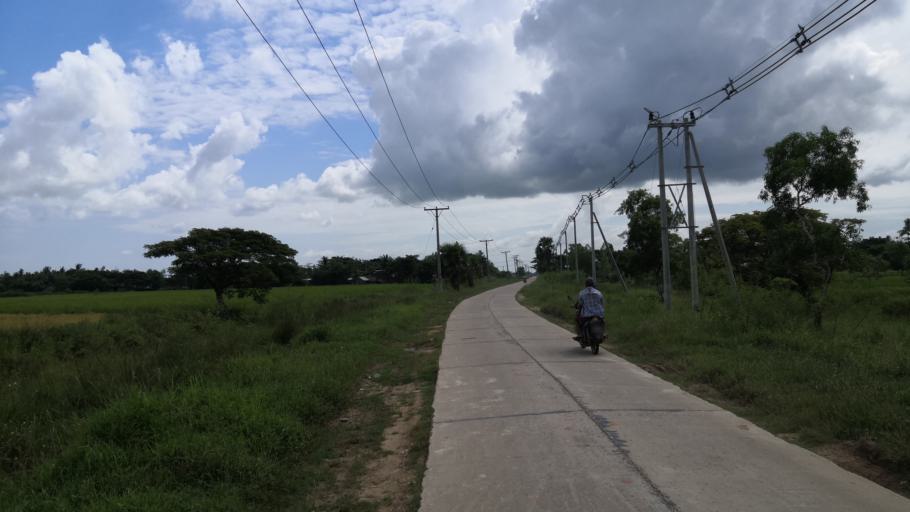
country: MM
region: Yangon
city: Kanbe
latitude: 16.4365
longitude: 96.1591
